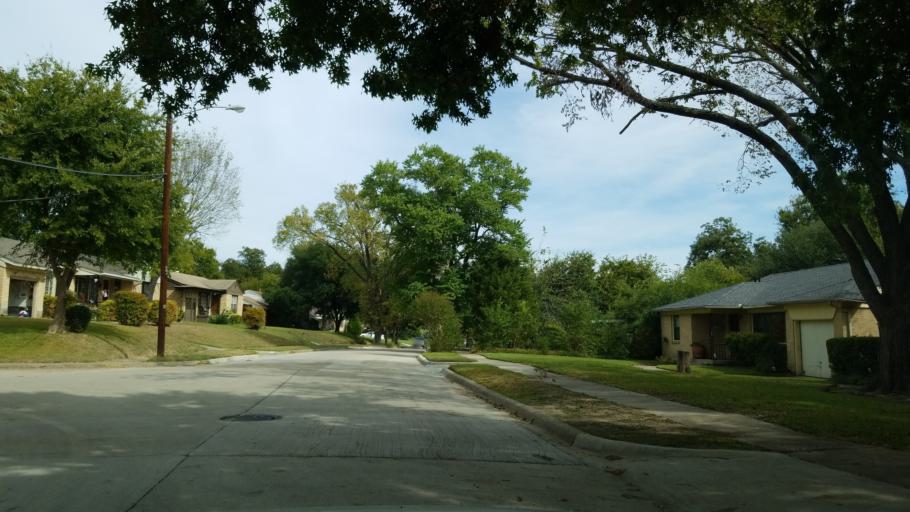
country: US
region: Texas
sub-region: Dallas County
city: Dallas
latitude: 32.7691
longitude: -96.7228
